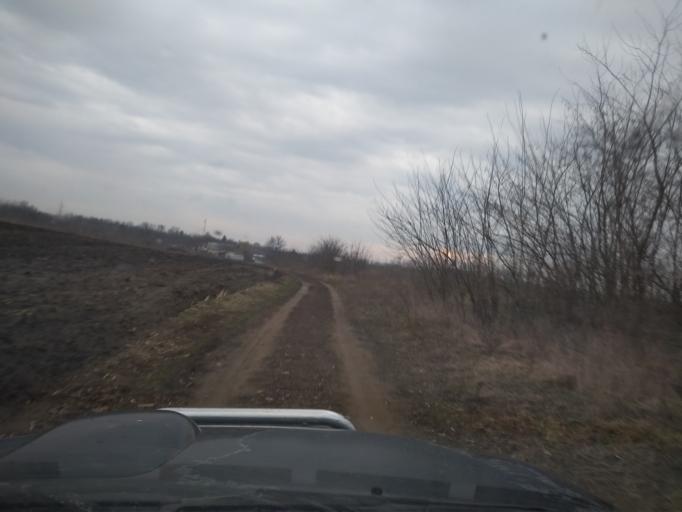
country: HU
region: Szabolcs-Szatmar-Bereg
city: Nagycserkesz
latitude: 47.9772
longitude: 21.5541
